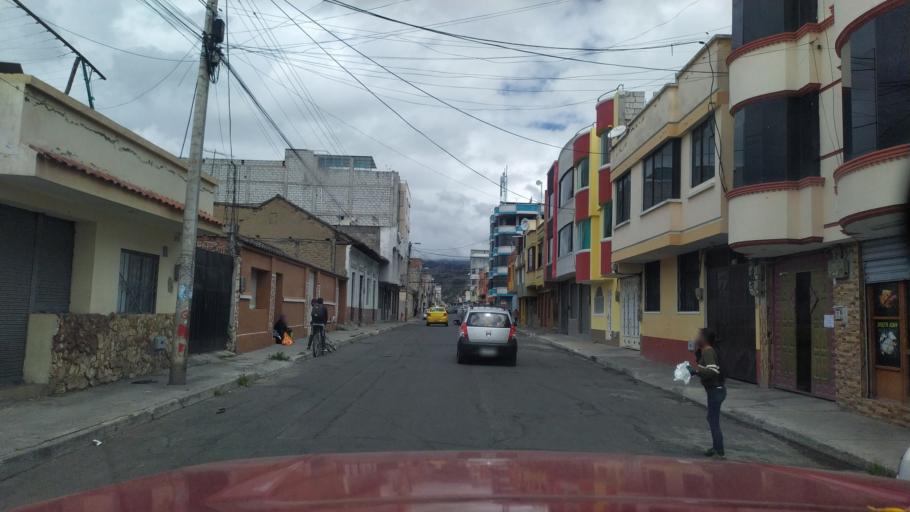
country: EC
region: Chimborazo
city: Riobamba
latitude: -1.6703
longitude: -78.6439
